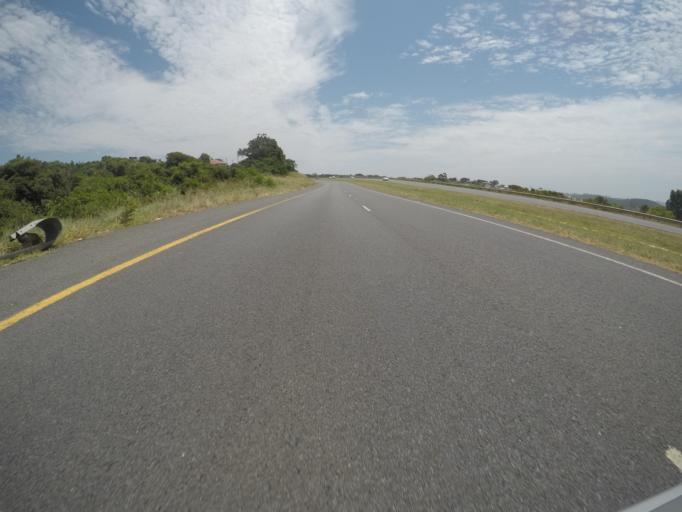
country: ZA
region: Eastern Cape
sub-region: Buffalo City Metropolitan Municipality
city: East London
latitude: -32.9694
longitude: 27.8806
